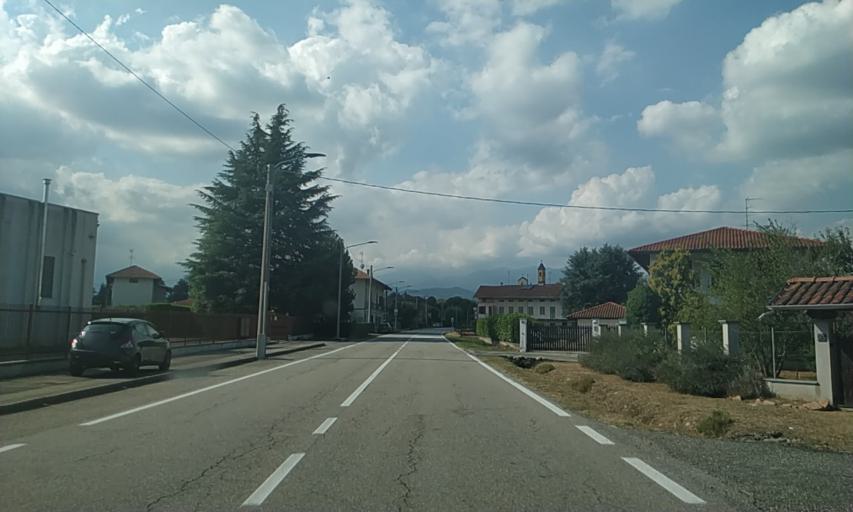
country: IT
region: Piedmont
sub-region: Provincia di Biella
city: Cerreto Castello
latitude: 45.5476
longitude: 8.1766
